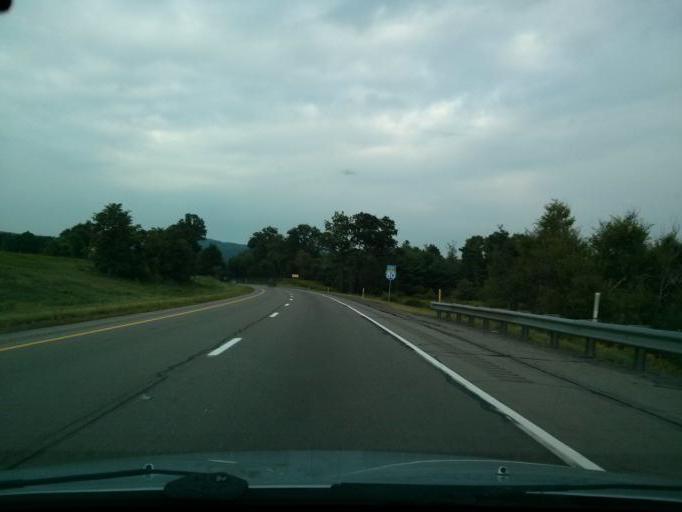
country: US
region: Pennsylvania
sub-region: Jefferson County
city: Brookville
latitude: 41.1676
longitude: -79.0415
